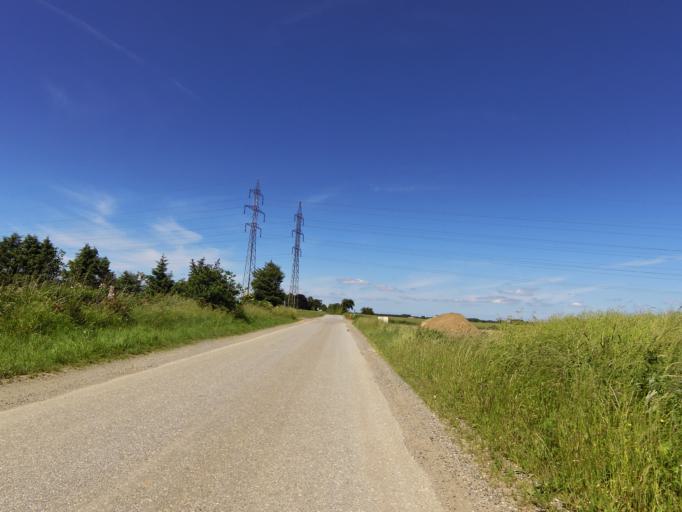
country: DK
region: South Denmark
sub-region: Aabenraa Kommune
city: Rodekro
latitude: 55.0372
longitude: 9.3024
